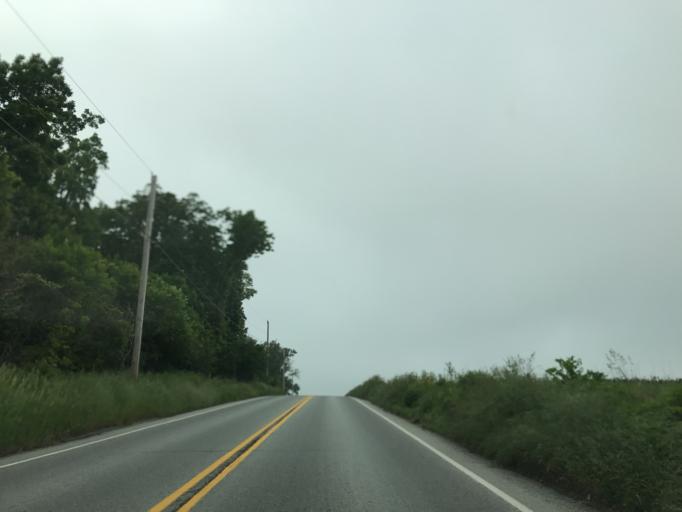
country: US
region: Pennsylvania
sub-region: York County
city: Susquehanna Trails
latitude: 39.8477
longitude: -76.4258
